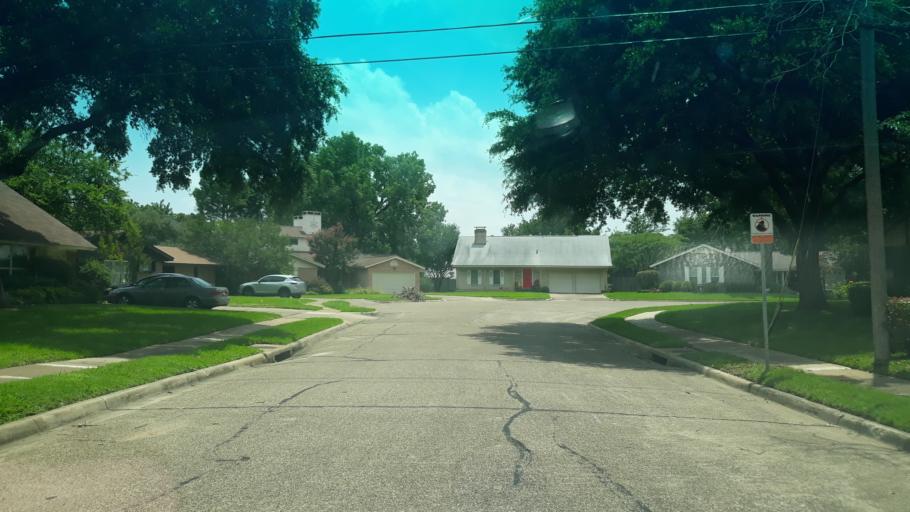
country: US
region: Texas
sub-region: Dallas County
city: Irving
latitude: 32.8561
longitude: -96.9613
